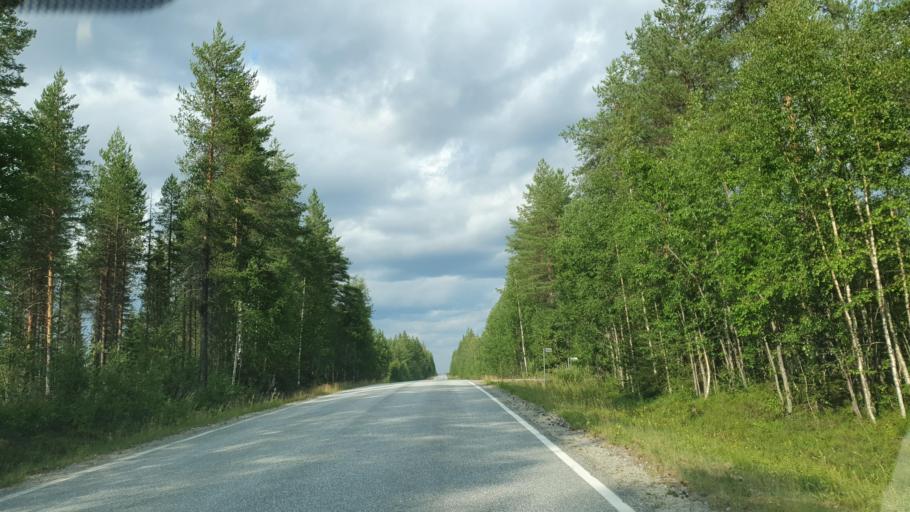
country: FI
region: Kainuu
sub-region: Kehys-Kainuu
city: Kuhmo
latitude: 64.4132
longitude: 29.4819
